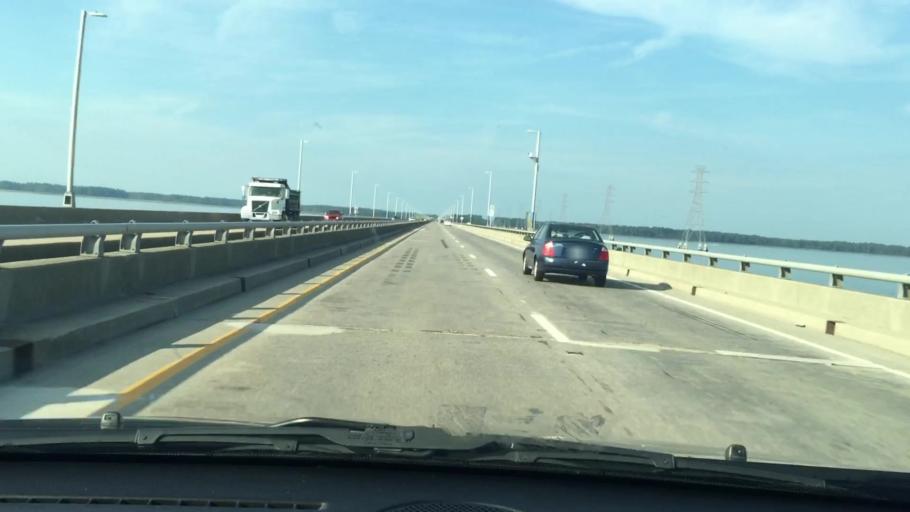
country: US
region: Virginia
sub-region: City of Newport News
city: Newport News
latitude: 36.9834
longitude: -76.4927
